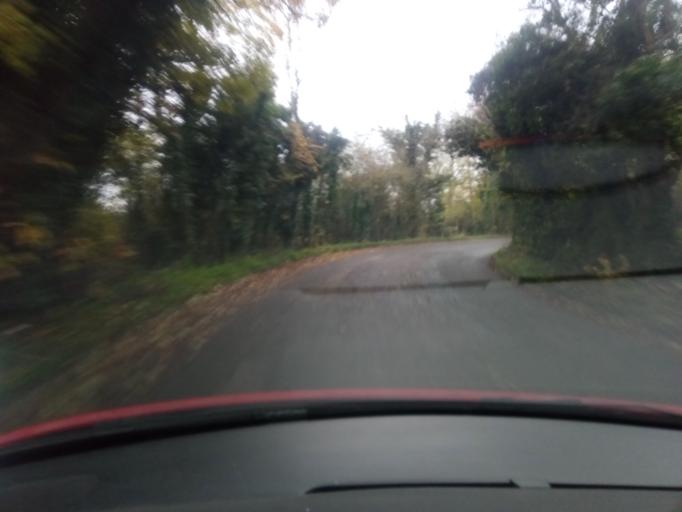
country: GB
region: England
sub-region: Derbyshire
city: Melbourne
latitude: 52.8693
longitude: -1.4281
